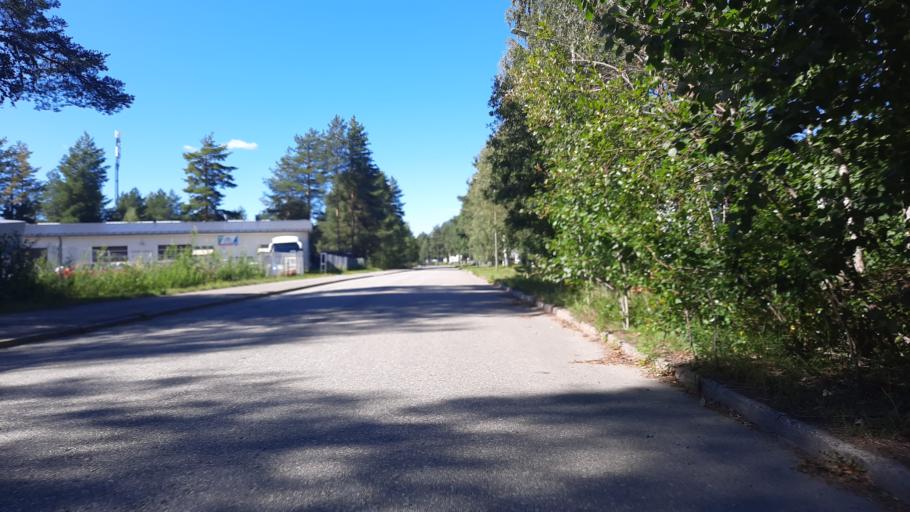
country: FI
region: North Karelia
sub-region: Joensuu
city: Joensuu
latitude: 62.6240
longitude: 29.7471
